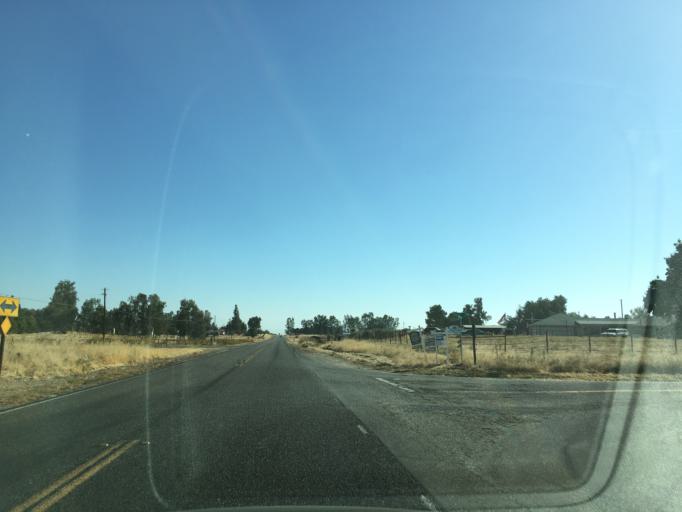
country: US
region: California
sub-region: Madera County
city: Parksdale
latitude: 36.9972
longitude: -119.9839
